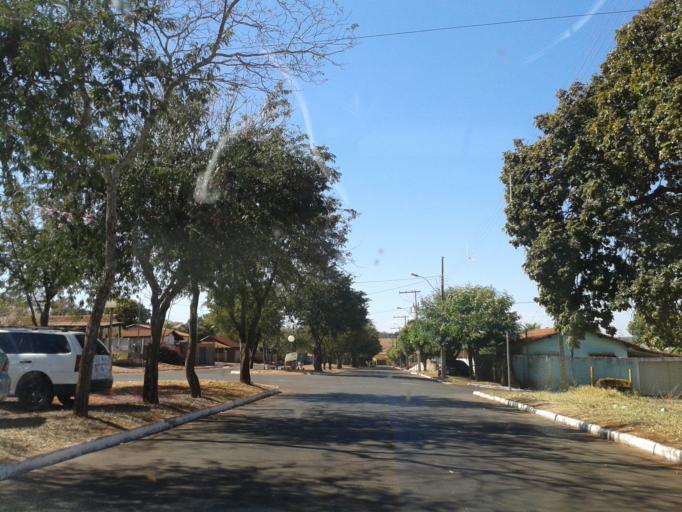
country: BR
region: Minas Gerais
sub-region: Santa Vitoria
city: Santa Vitoria
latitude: -18.8380
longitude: -50.1319
